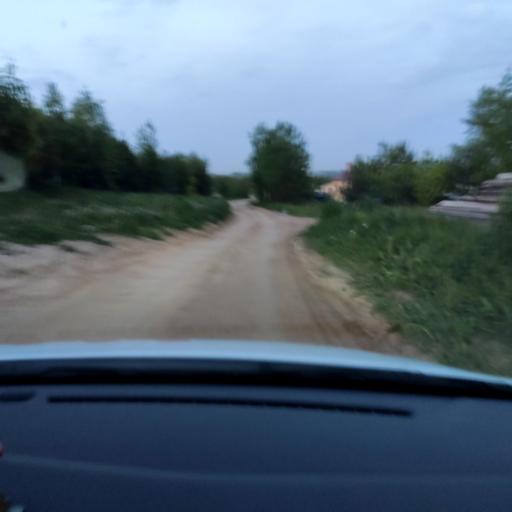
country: RU
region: Tatarstan
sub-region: Gorod Kazan'
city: Kazan
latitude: 55.8833
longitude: 49.1039
